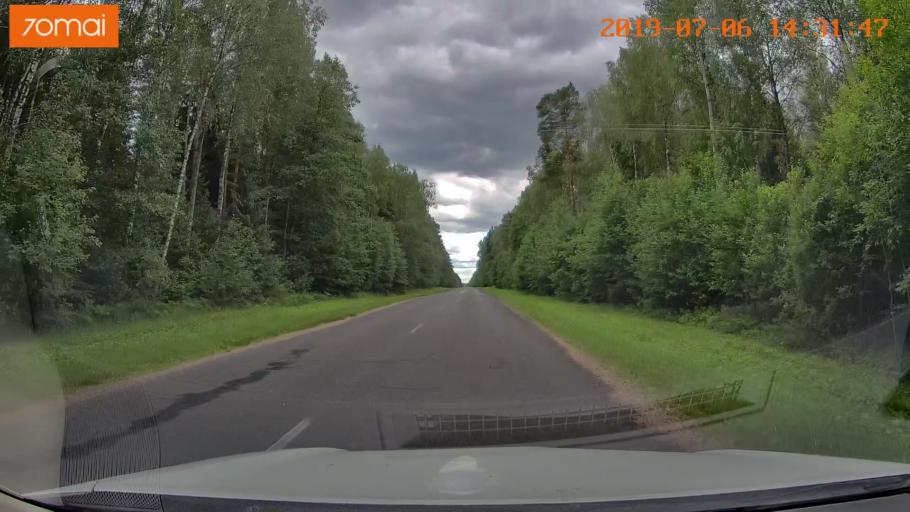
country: BY
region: Minsk
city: Ivyanyets
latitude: 53.9147
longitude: 26.7667
